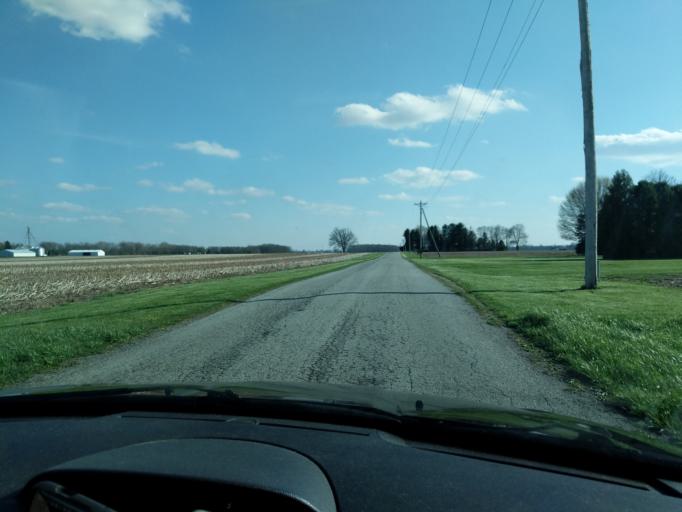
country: US
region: Ohio
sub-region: Champaign County
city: Urbana
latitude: 40.1435
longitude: -83.8153
